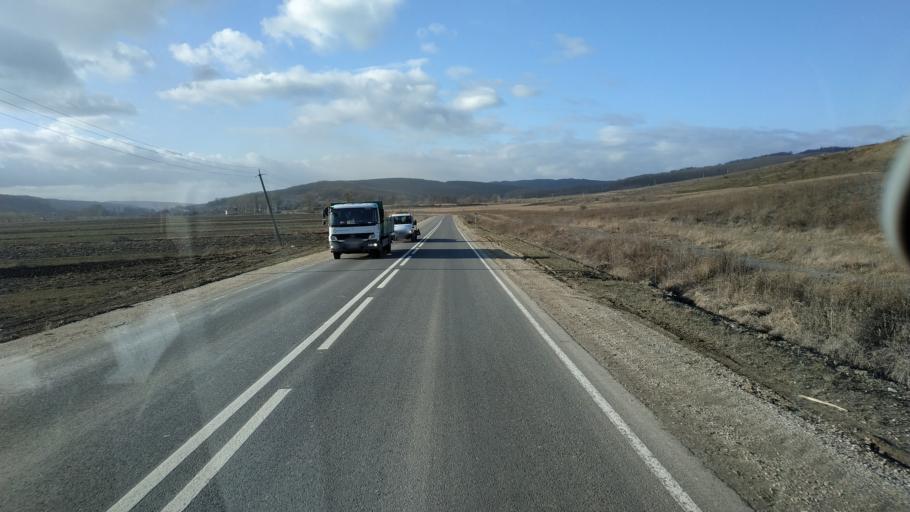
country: MD
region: Calarasi
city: Calarasi
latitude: 47.3245
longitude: 28.1040
